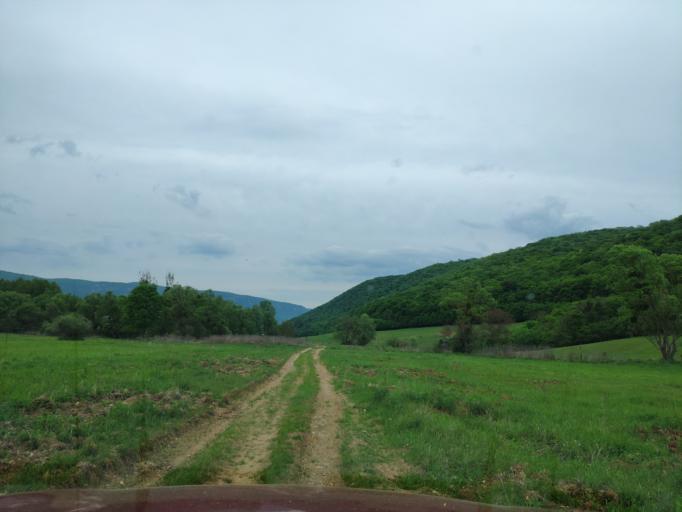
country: SK
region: Kosicky
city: Roznava
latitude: 48.5620
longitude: 20.6347
